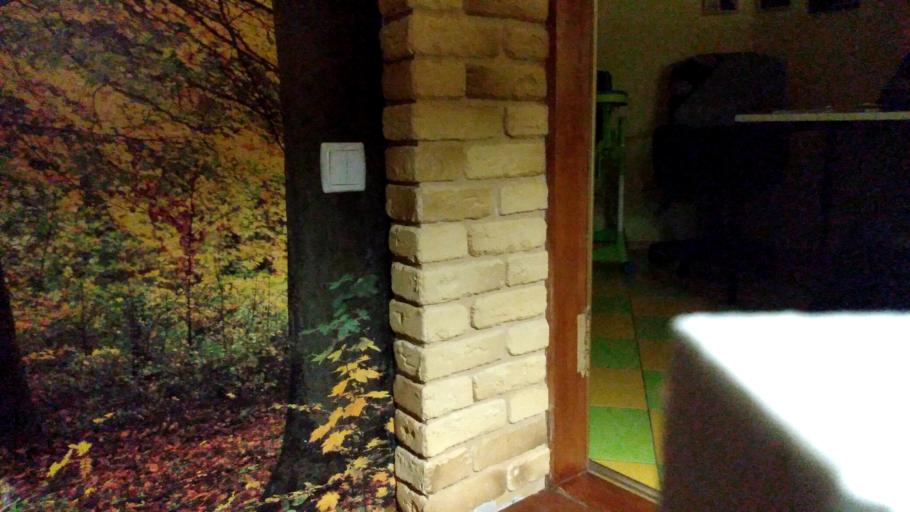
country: RU
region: Arkhangelskaya
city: Kargopol'
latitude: 61.4487
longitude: 37.7987
